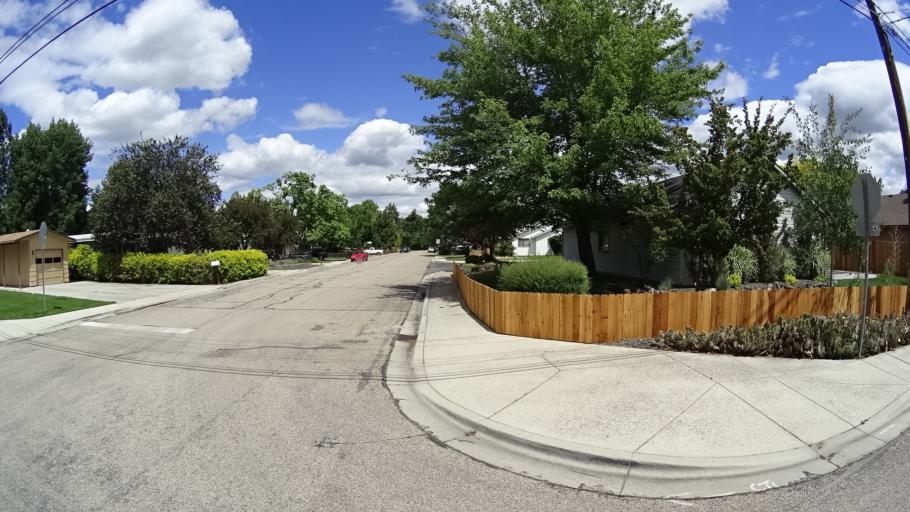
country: US
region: Idaho
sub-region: Ada County
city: Boise
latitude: 43.5843
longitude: -116.1871
